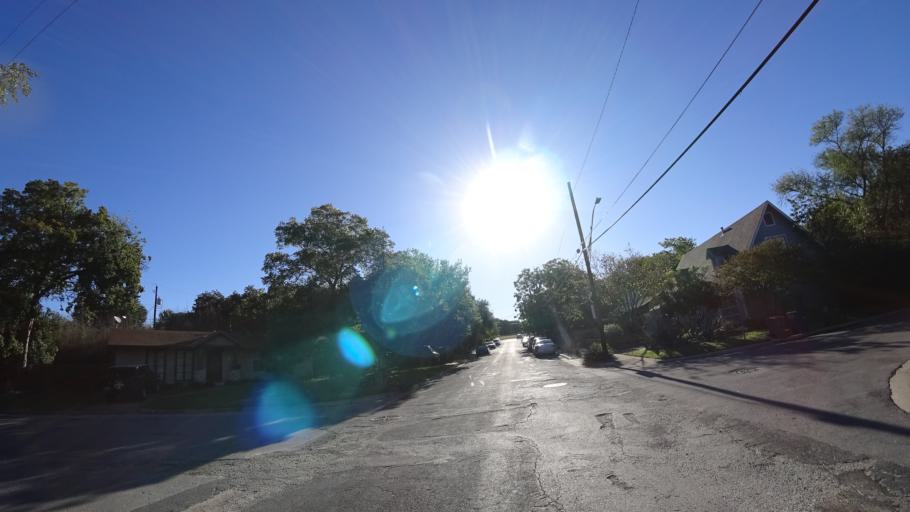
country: US
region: Texas
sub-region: Travis County
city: Austin
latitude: 30.2325
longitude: -97.7605
